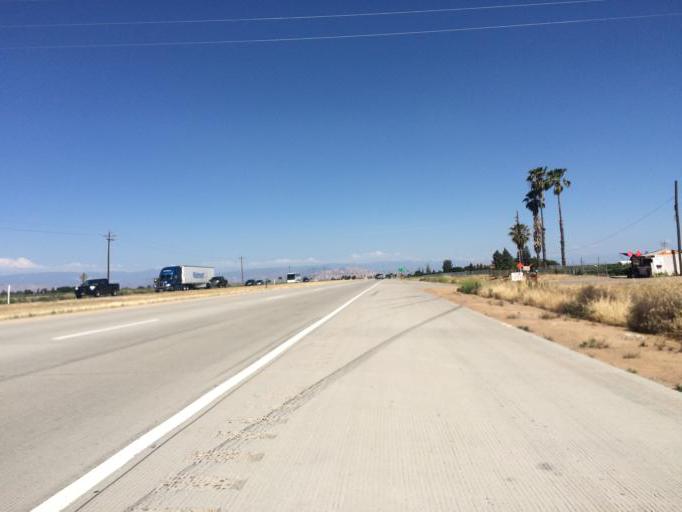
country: US
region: California
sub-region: Fresno County
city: Sunnyside
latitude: 36.7367
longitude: -119.6432
